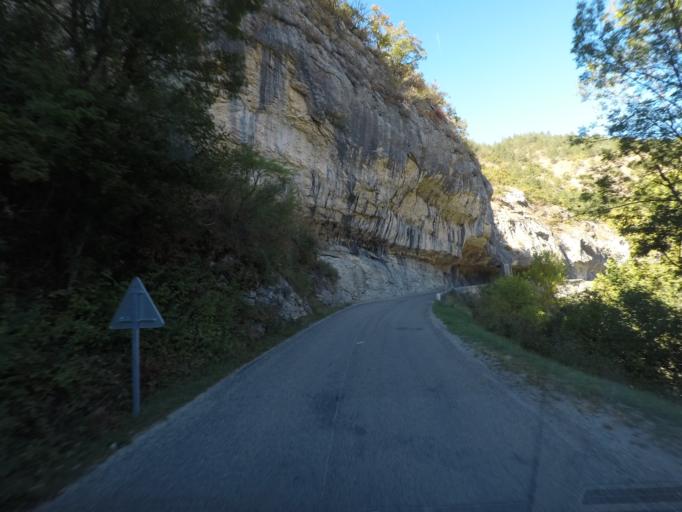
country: FR
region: Rhone-Alpes
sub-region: Departement de la Drome
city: Die
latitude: 44.6536
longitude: 5.2837
